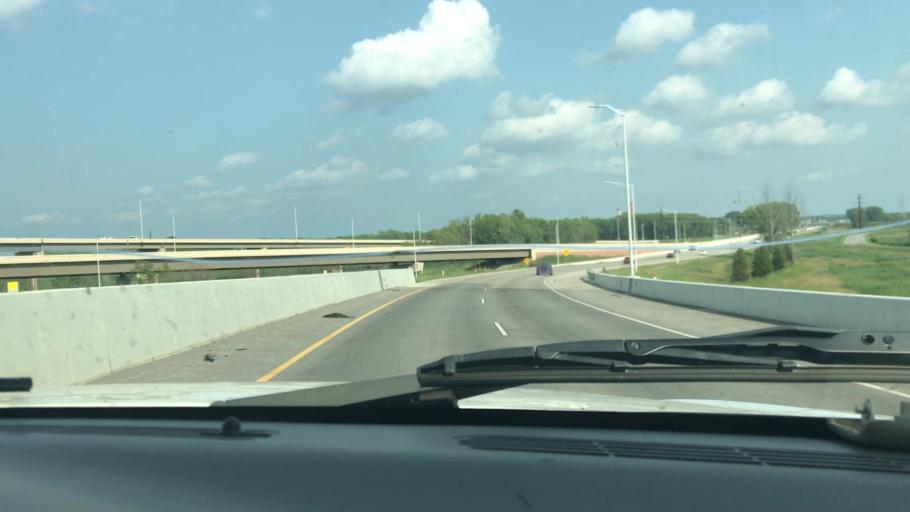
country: US
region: Wisconsin
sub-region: Brown County
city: Howard
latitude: 44.5589
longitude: -88.0523
